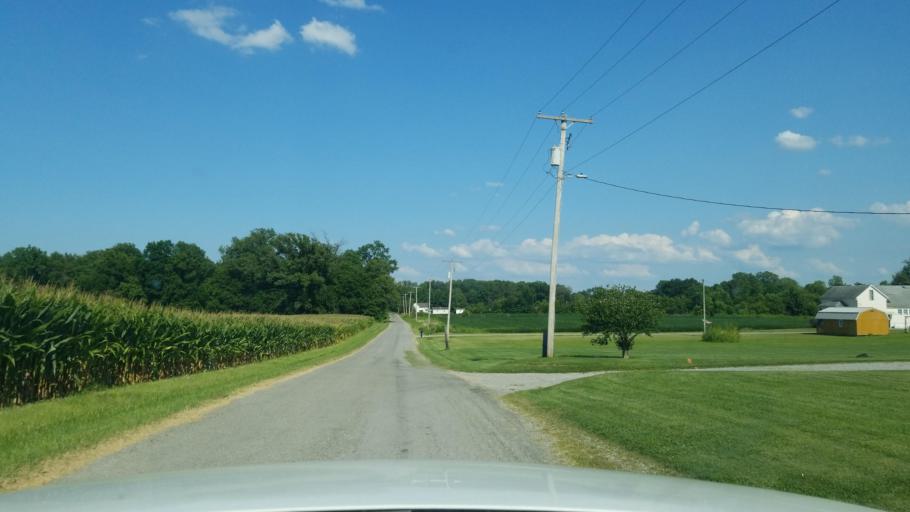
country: US
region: Illinois
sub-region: Saline County
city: Eldorado
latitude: 37.7864
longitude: -88.4945
